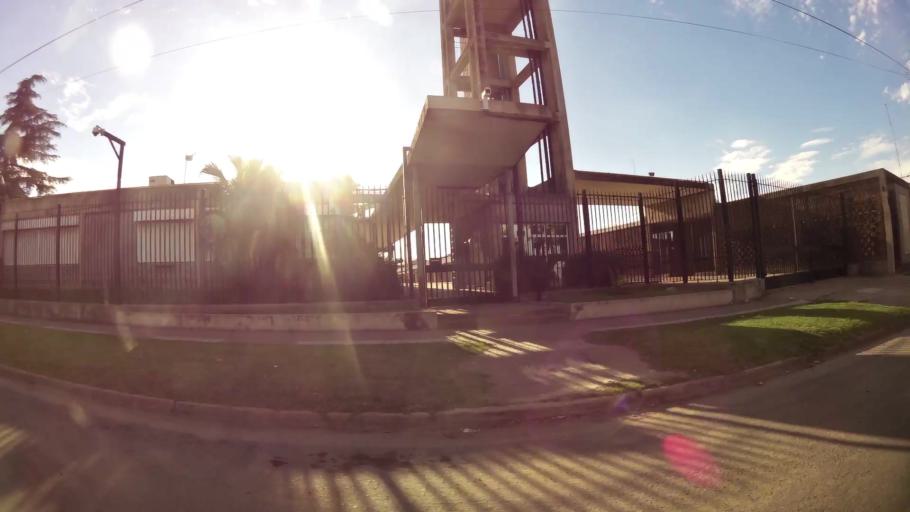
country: AR
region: Santa Fe
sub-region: Departamento de Rosario
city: Rosario
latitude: -32.9874
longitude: -60.6725
